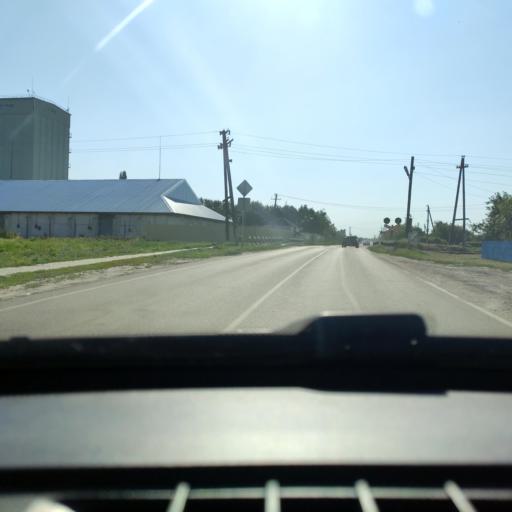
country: RU
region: Voronezj
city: Panino
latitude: 51.6441
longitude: 40.1307
